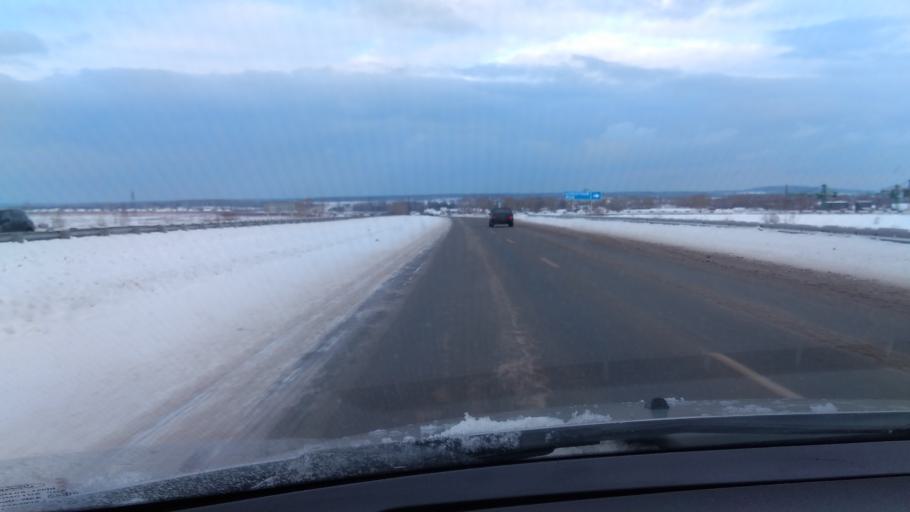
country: RU
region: Sverdlovsk
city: Tsementnyy
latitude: 57.4818
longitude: 60.1803
